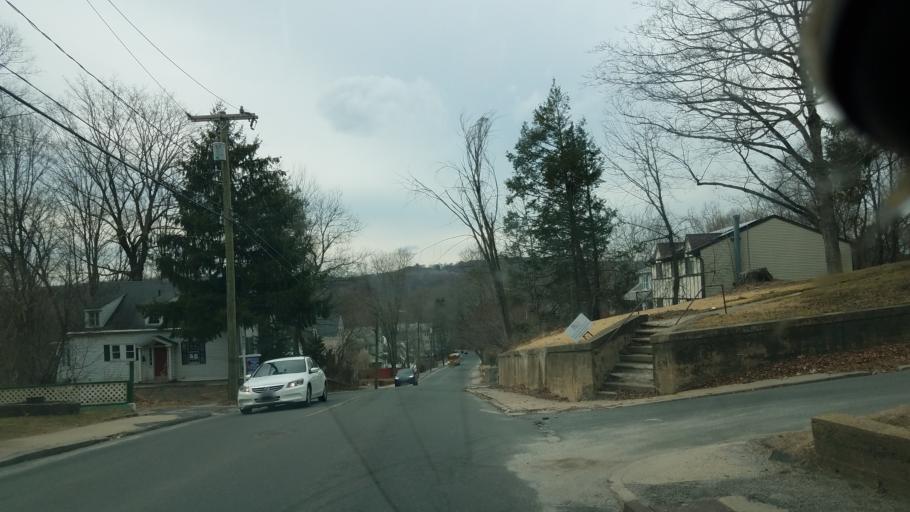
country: US
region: Connecticut
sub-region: New Haven County
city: Waterbury
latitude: 41.5880
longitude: -73.0440
